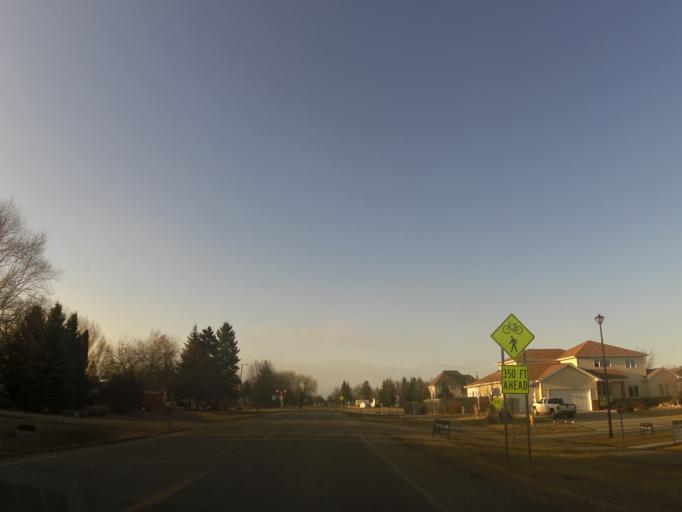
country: US
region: North Dakota
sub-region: Grand Forks County
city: Grand Forks
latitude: 47.8694
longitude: -97.0291
